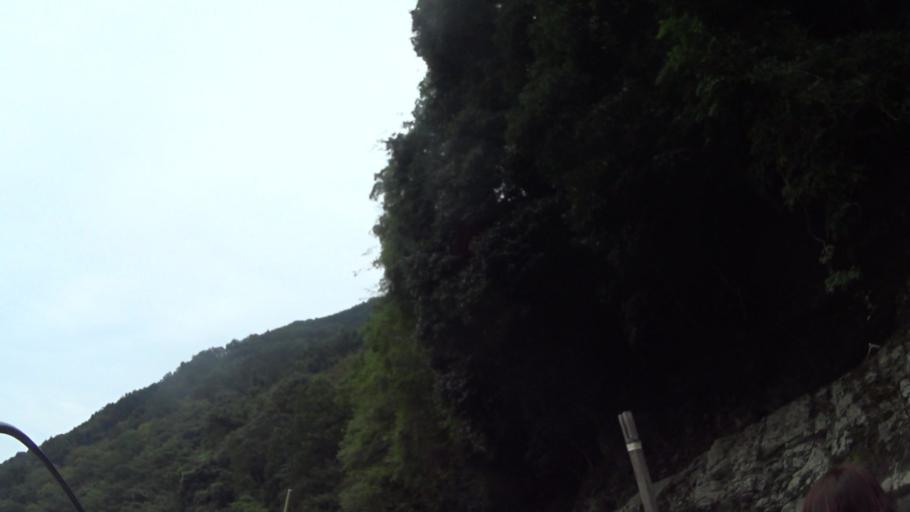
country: JP
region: Kyoto
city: Muko
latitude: 35.0179
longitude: 135.6586
